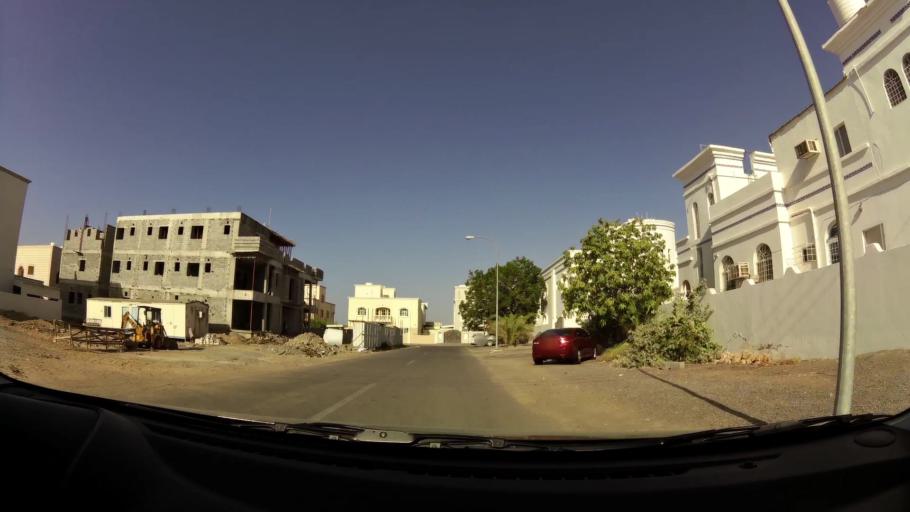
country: OM
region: Muhafazat Masqat
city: As Sib al Jadidah
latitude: 23.6006
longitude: 58.2157
